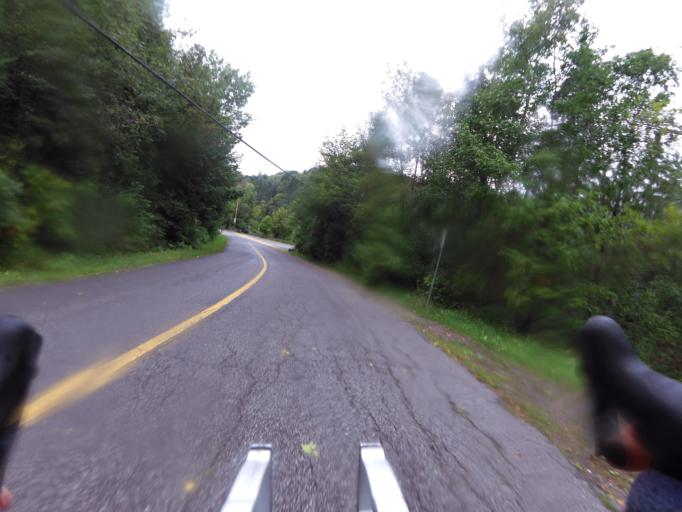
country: CA
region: Quebec
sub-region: Outaouais
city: Wakefield
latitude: 45.6462
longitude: -75.9176
